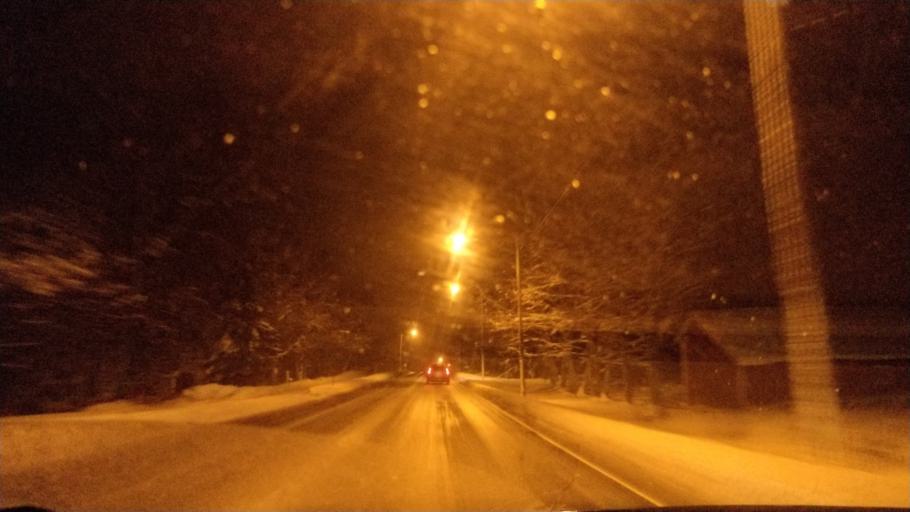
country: FI
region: Lapland
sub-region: Rovaniemi
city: Rovaniemi
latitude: 66.2640
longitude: 25.3379
